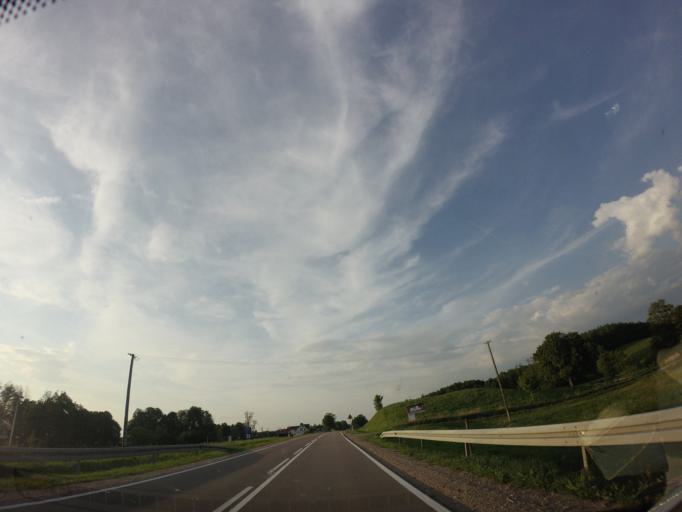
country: LT
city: Lazdijai
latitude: 54.1438
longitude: 23.4672
